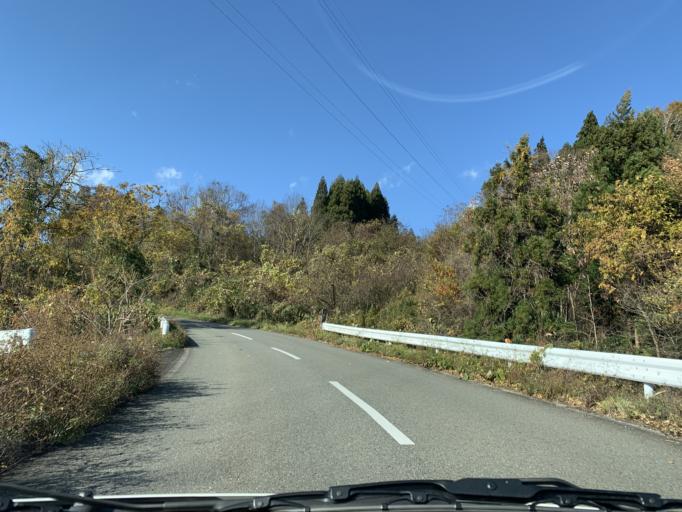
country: JP
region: Iwate
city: Mizusawa
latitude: 39.0925
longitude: 141.1248
